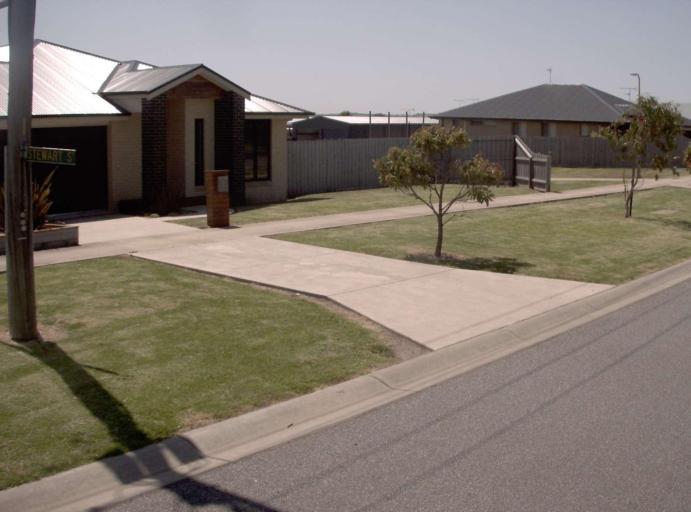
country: AU
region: Victoria
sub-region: Bass Coast
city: North Wonthaggi
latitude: -38.6154
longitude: 145.5970
